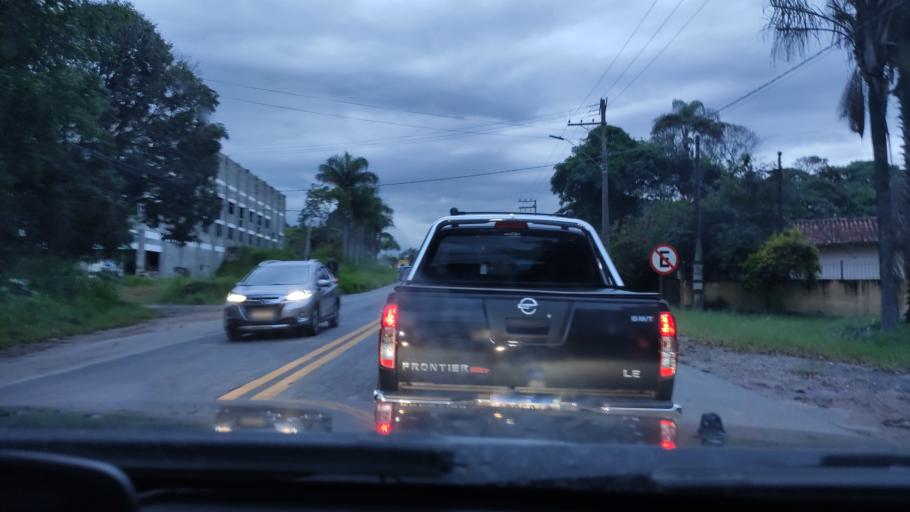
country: BR
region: Sao Paulo
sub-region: Socorro
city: Socorro
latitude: -22.5708
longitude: -46.5343
